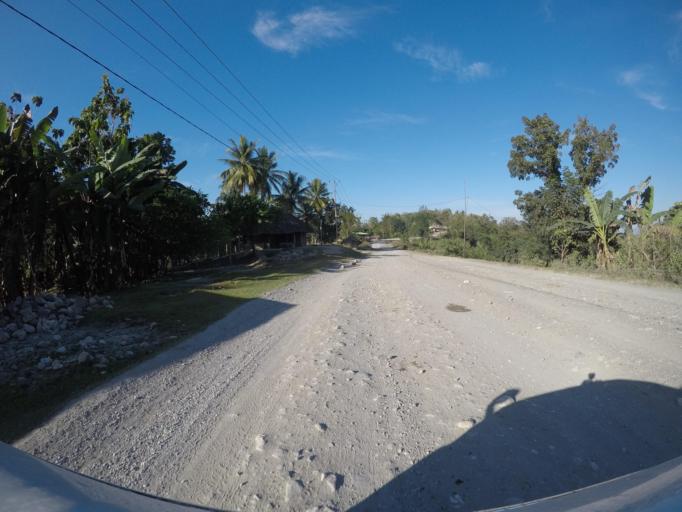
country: TL
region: Viqueque
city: Viqueque
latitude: -8.8691
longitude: 126.3291
